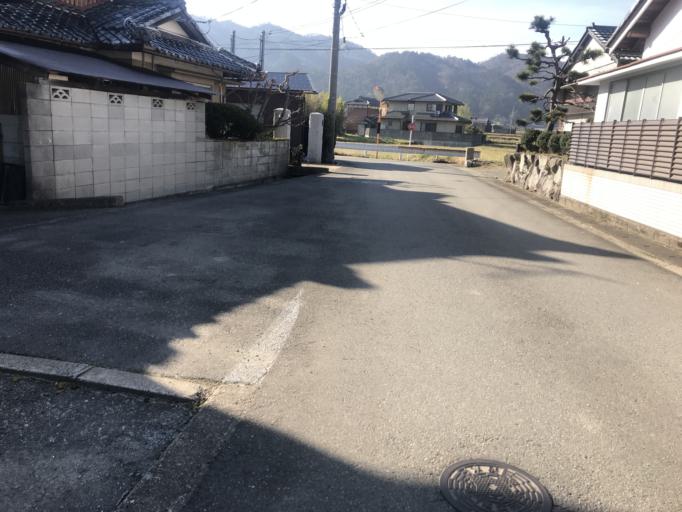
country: JP
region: Kyoto
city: Kameoka
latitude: 34.9853
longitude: 135.5400
